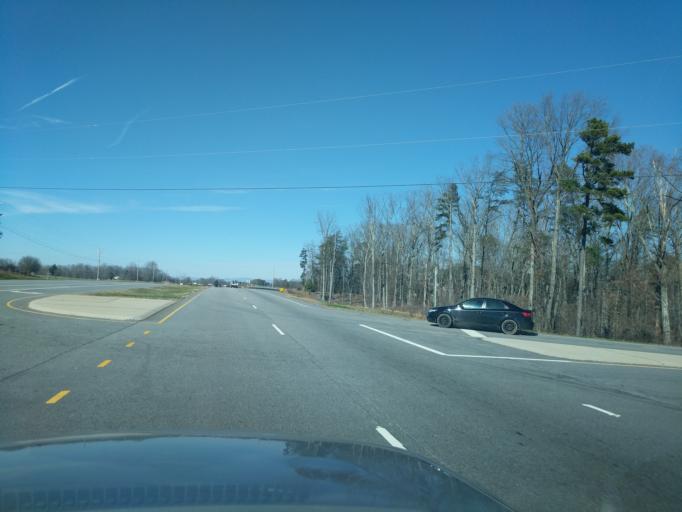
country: US
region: North Carolina
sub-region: Rutherford County
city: Forest City
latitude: 35.2623
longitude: -81.8844
